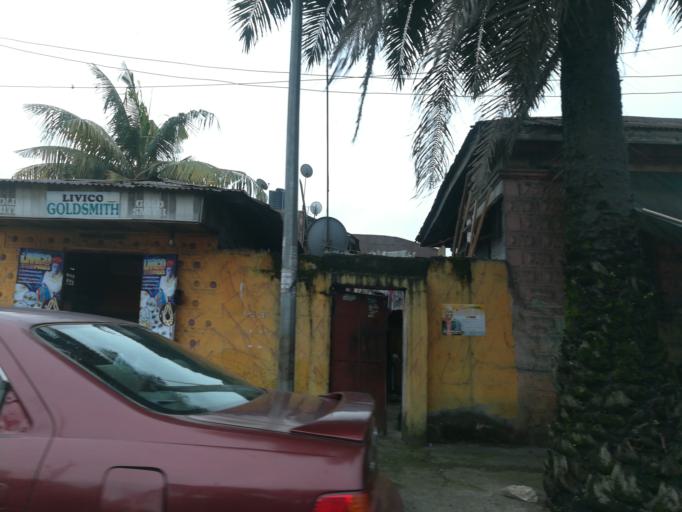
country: NG
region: Rivers
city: Port Harcourt
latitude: 4.7607
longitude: 7.0259
